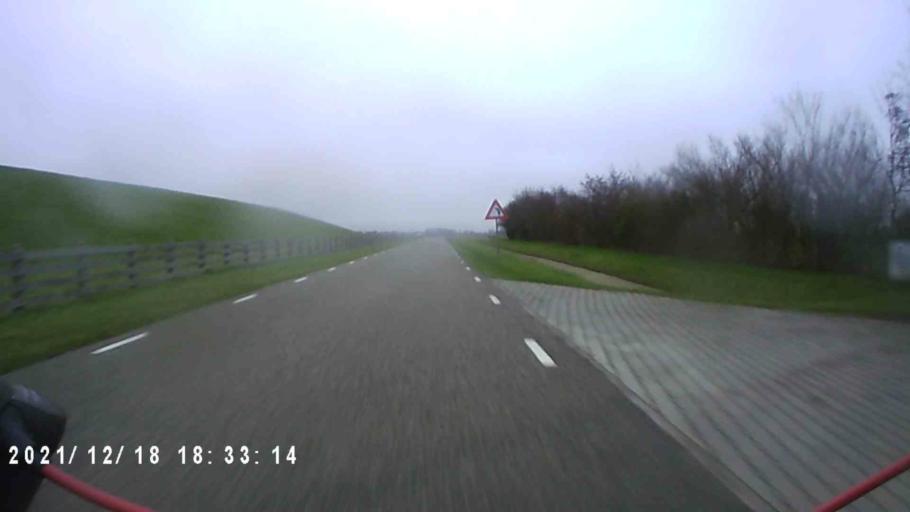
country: NL
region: Friesland
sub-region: Gemeente Dongeradeel
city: Ternaard
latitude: 53.4016
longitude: 6.0215
